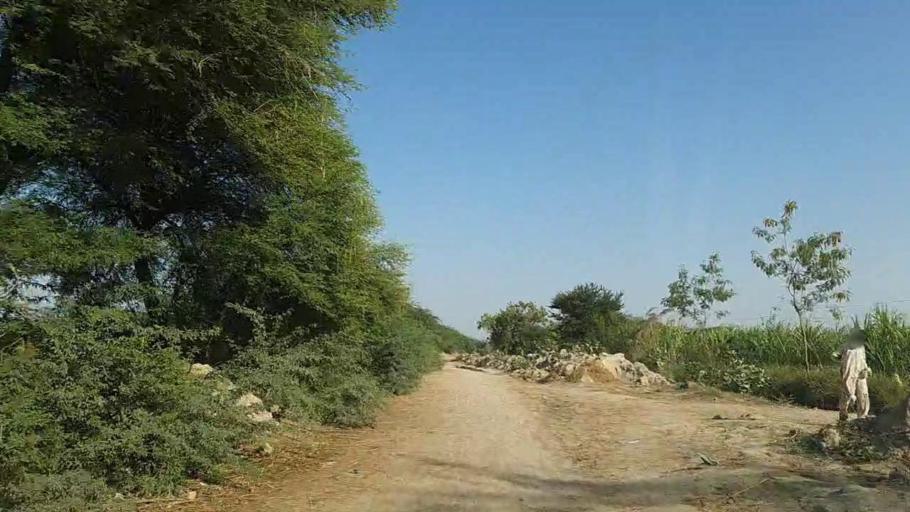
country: PK
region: Sindh
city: Chuhar Jamali
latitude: 24.5715
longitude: 68.0369
